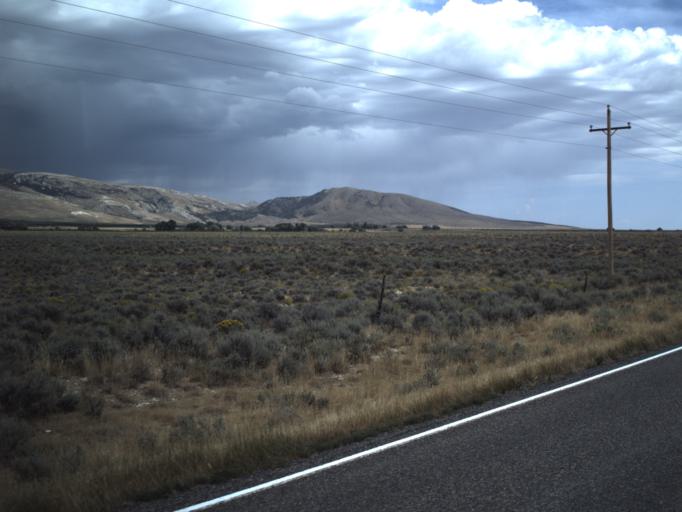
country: US
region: Idaho
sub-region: Cassia County
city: Burley
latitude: 41.8166
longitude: -113.3621
